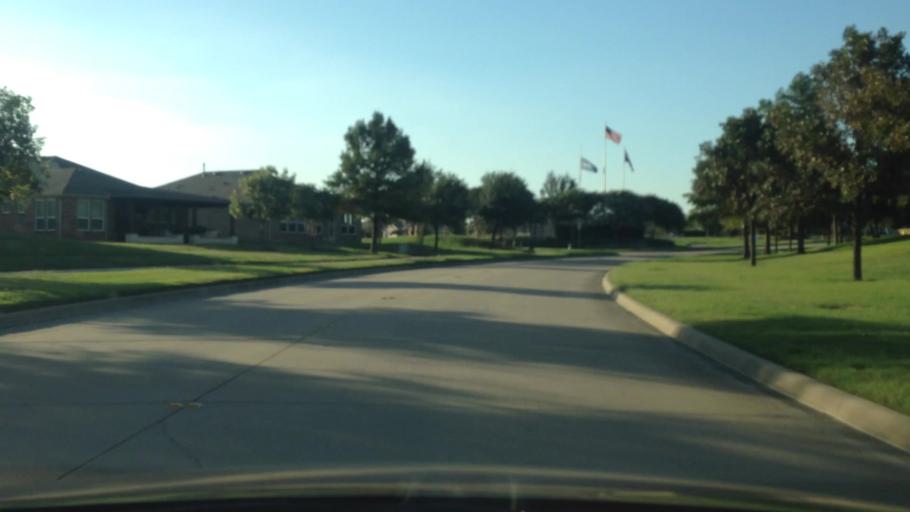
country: US
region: Texas
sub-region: Denton County
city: Little Elm
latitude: 33.1375
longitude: -96.8977
